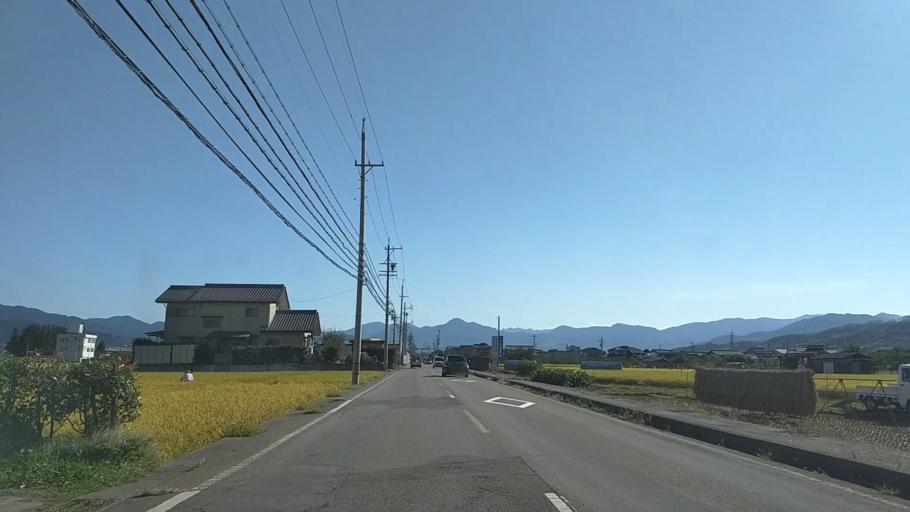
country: JP
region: Nagano
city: Nagano-shi
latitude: 36.6063
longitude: 138.1431
